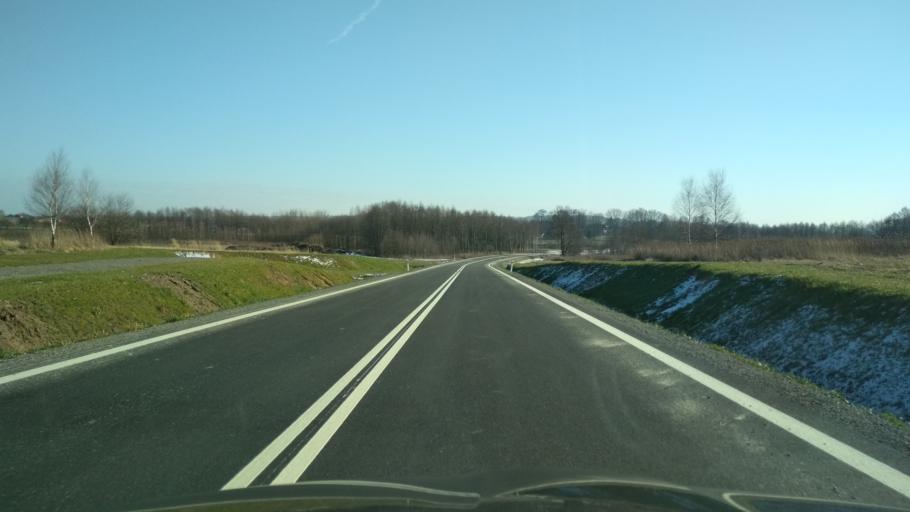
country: PL
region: Subcarpathian Voivodeship
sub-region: Powiat ropczycko-sedziszowski
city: Sedziszow Malopolski
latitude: 50.0747
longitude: 21.7290
